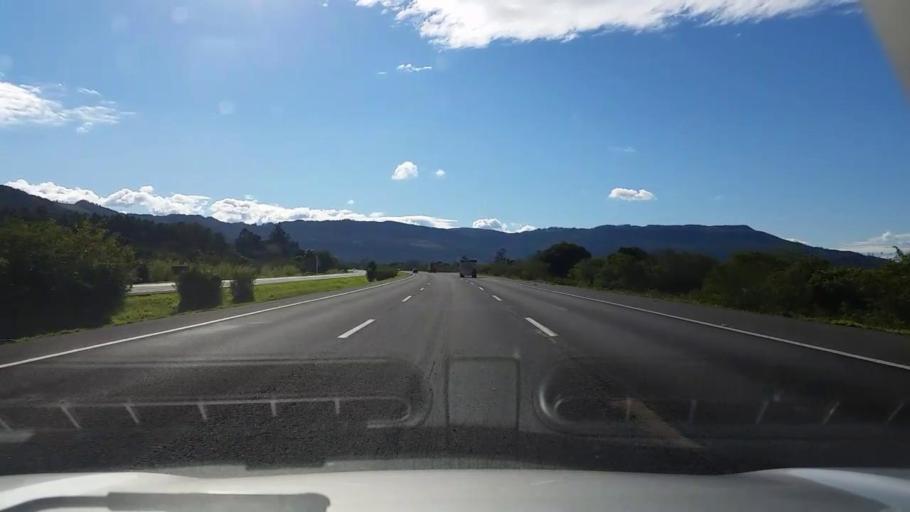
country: BR
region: Rio Grande do Sul
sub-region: Osorio
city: Osorio
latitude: -29.8815
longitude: -50.4354
